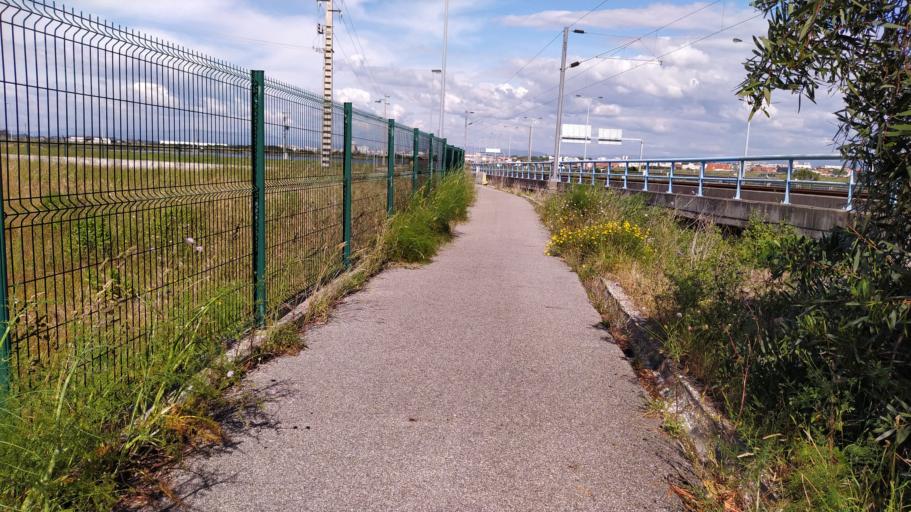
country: PT
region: Aveiro
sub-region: Ilhavo
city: Gafanha da Nazare
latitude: 40.6332
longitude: -8.6832
